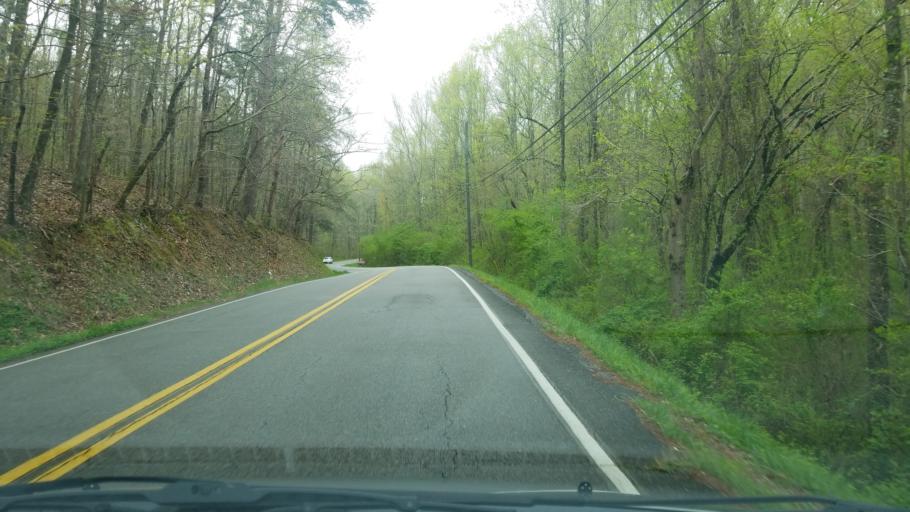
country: US
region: Tennessee
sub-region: Hamilton County
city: Collegedale
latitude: 35.0202
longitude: -85.0713
